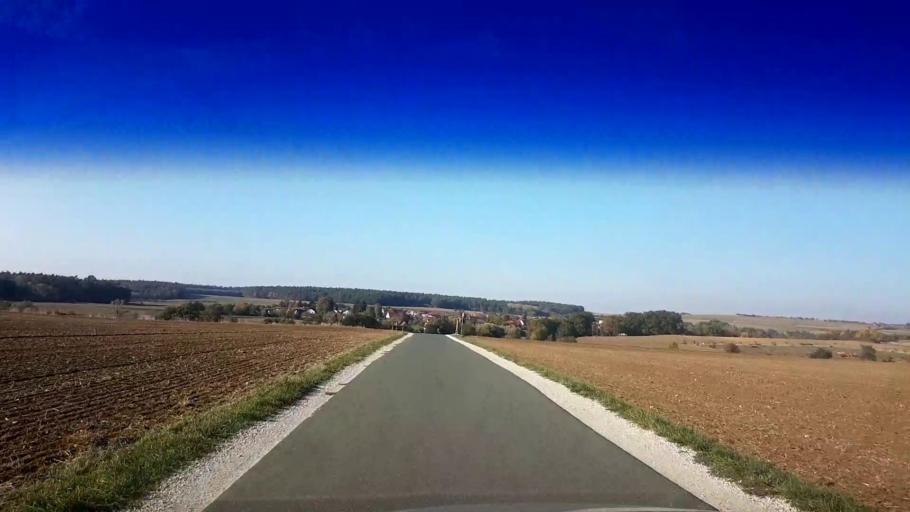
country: DE
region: Bavaria
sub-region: Upper Franconia
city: Strullendorf
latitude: 49.8582
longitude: 10.9999
